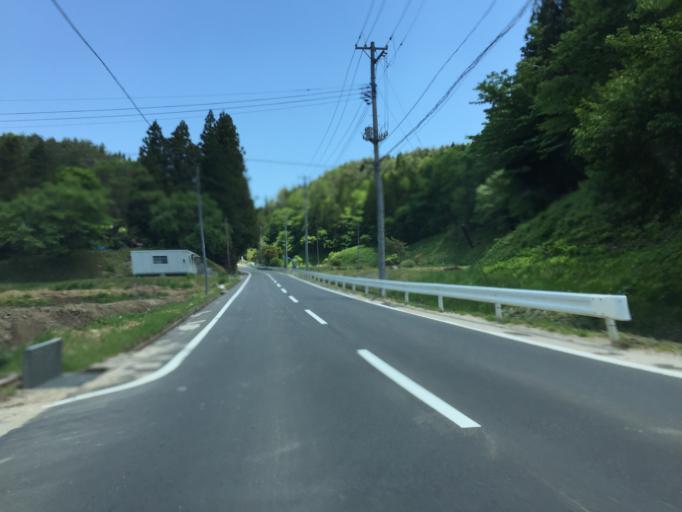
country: JP
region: Fukushima
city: Funehikimachi-funehiki
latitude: 37.5126
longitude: 140.6812
